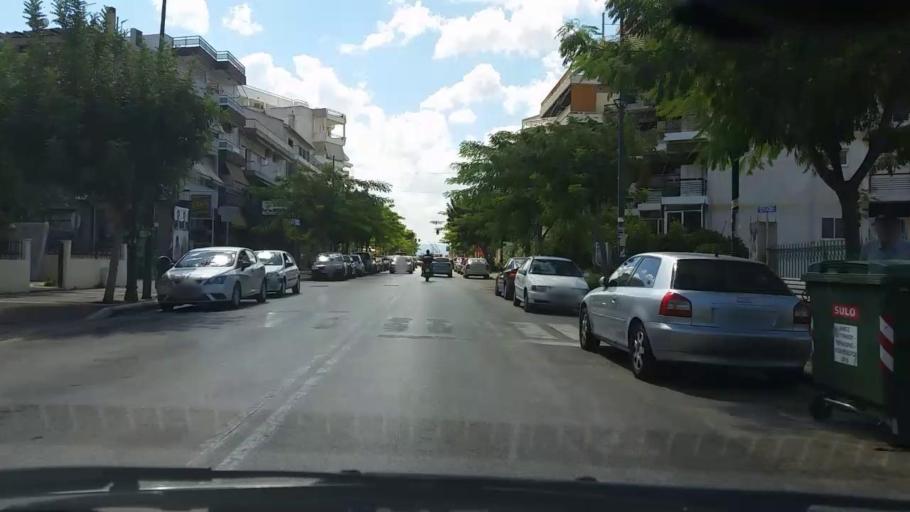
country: GR
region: Peloponnese
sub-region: Nomos Korinthias
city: Loutraki
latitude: 37.9710
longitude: 22.9779
